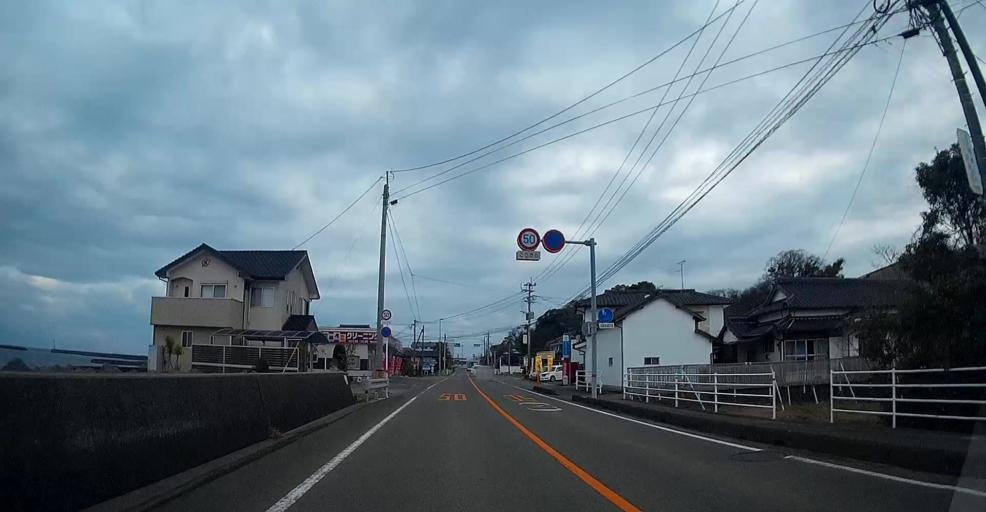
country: JP
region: Kumamoto
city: Hondo
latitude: 32.4704
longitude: 130.2512
